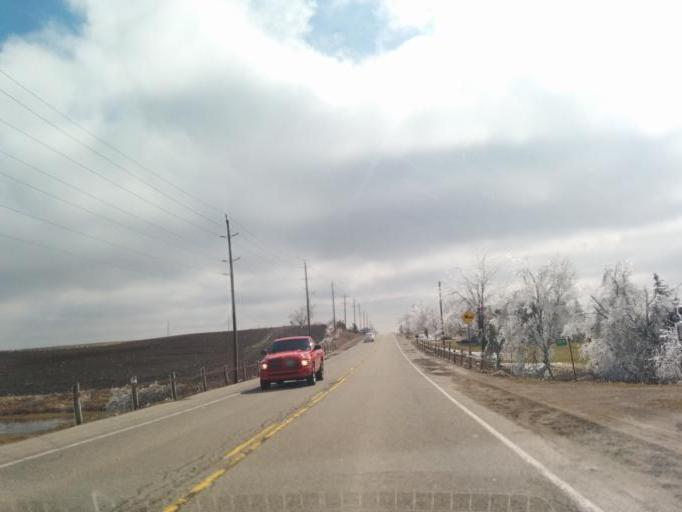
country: CA
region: Ontario
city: Waterloo
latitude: 43.6372
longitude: -80.5492
